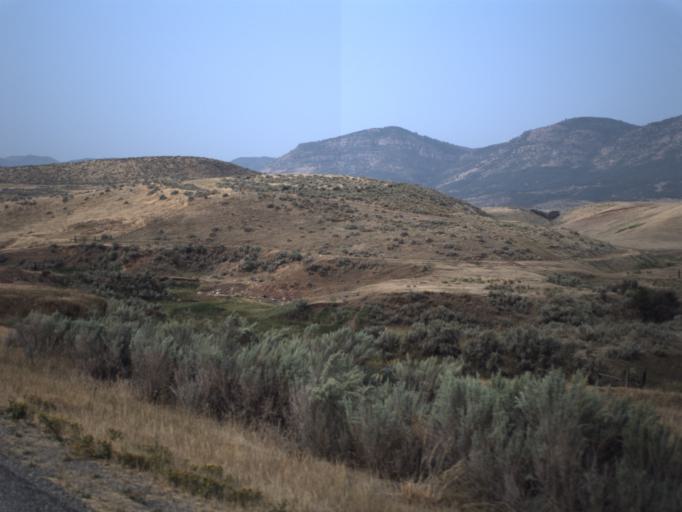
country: US
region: Utah
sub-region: Summit County
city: Coalville
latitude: 41.0123
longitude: -111.5156
